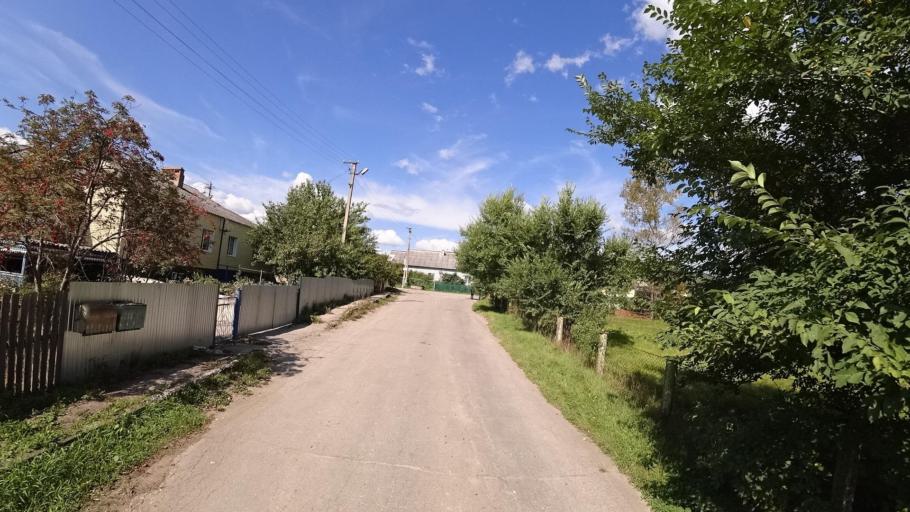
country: RU
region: Jewish Autonomous Oblast
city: Londoko
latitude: 49.0170
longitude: 131.8872
